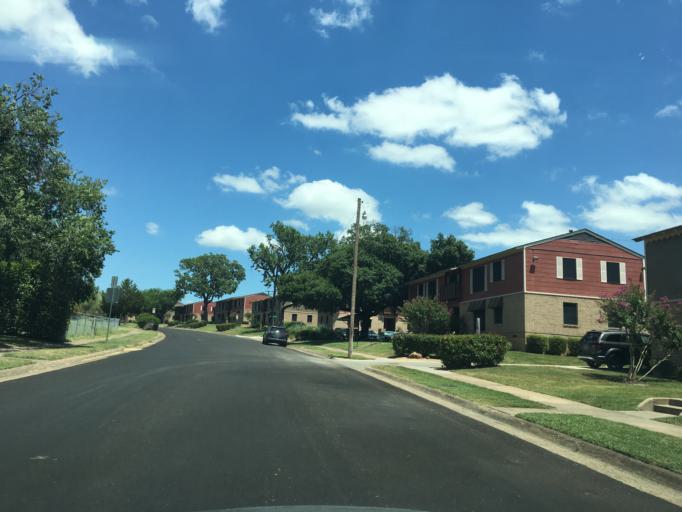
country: US
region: Texas
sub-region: Dallas County
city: Garland
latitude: 32.8472
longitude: -96.6899
